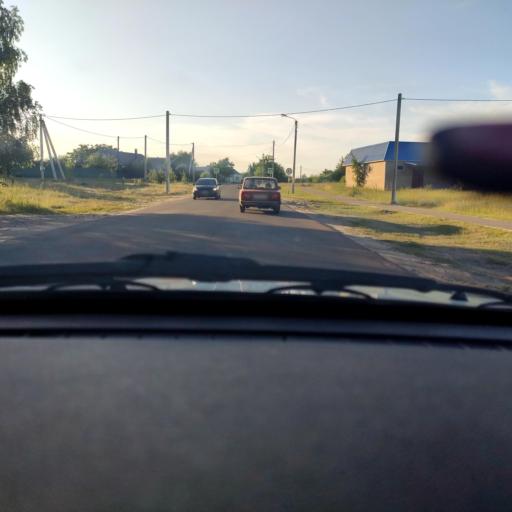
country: RU
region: Voronezj
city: Ramon'
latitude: 51.9006
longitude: 39.2866
